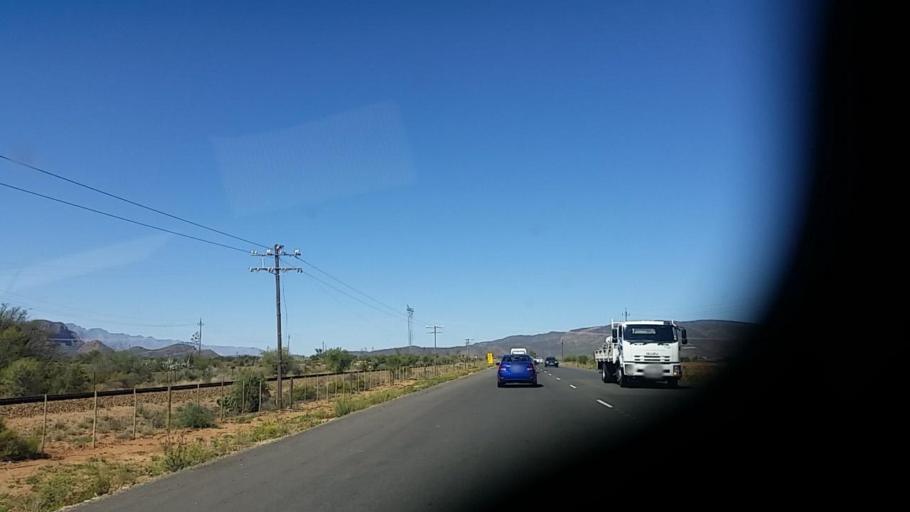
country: ZA
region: Western Cape
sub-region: Eden District Municipality
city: Oudtshoorn
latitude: -33.5609
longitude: 22.3911
